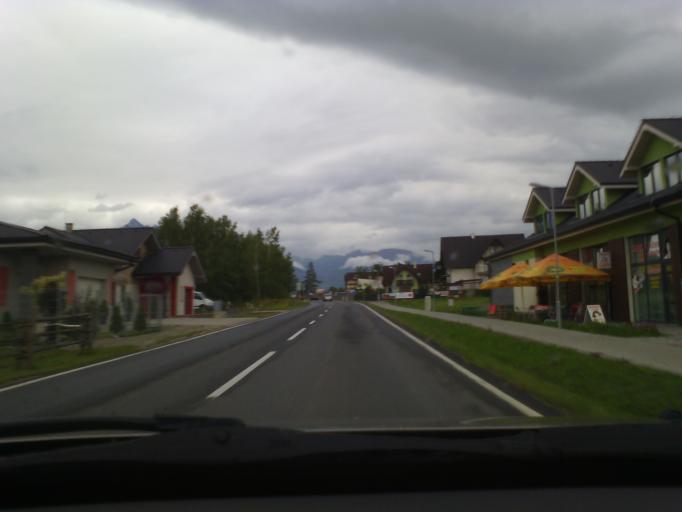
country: SK
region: Presovsky
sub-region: Okres Poprad
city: Poprad
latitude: 49.1203
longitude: 20.3517
